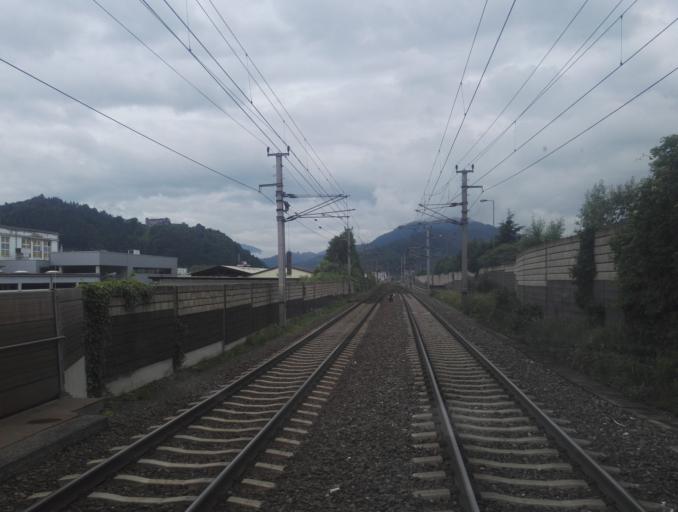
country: AT
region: Styria
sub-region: Politischer Bezirk Bruck-Muerzzuschlag
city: Kapfenberg
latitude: 47.4496
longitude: 15.3045
